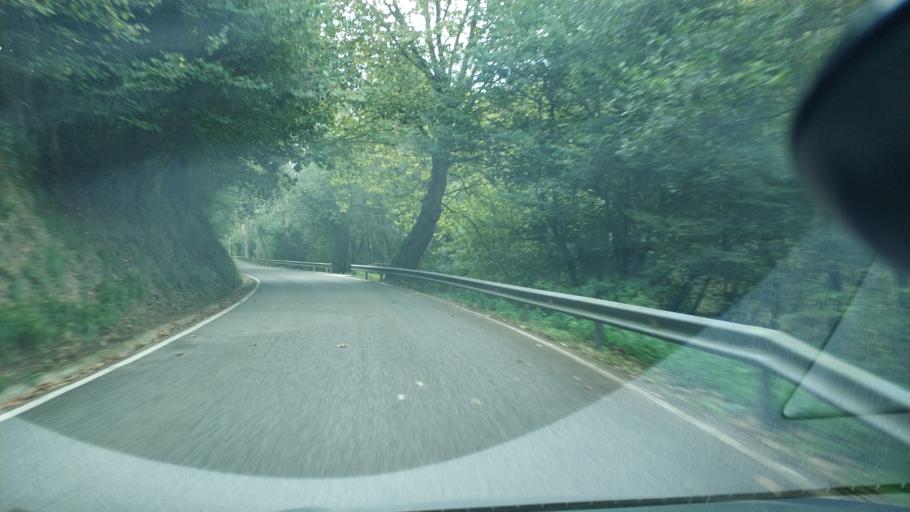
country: ES
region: Cantabria
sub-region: Provincia de Cantabria
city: Santa Maria de Cayon
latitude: 43.2849
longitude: -3.8159
